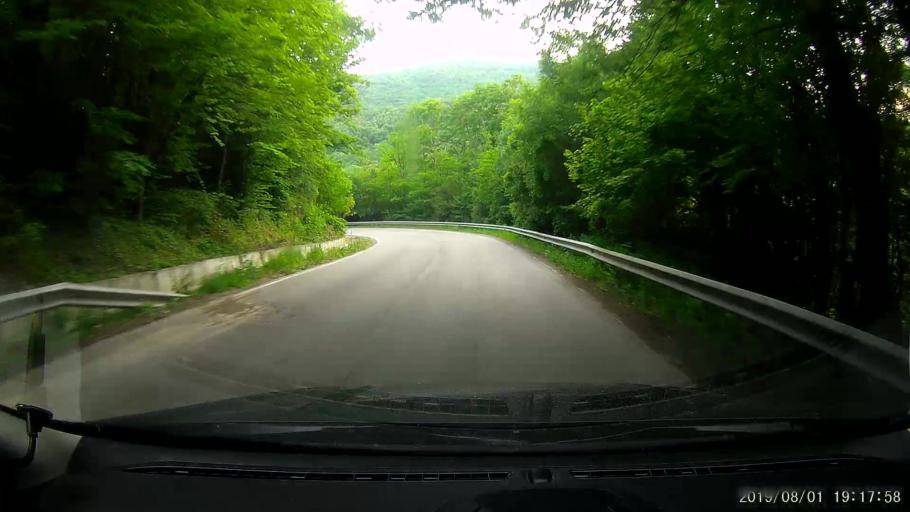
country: BG
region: Shumen
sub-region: Obshtina Smyadovo
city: Smyadovo
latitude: 42.9184
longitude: 26.9392
